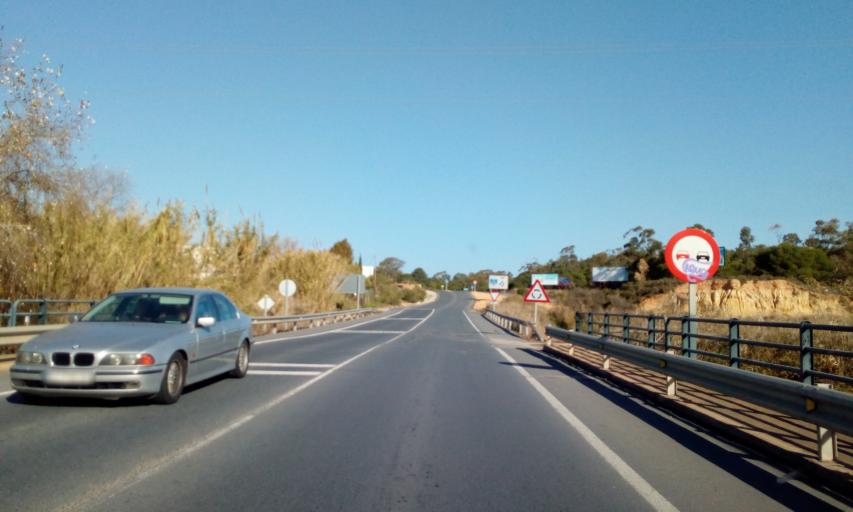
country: ES
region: Andalusia
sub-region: Provincia de Huelva
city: Lepe
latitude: 37.2111
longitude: -7.2179
